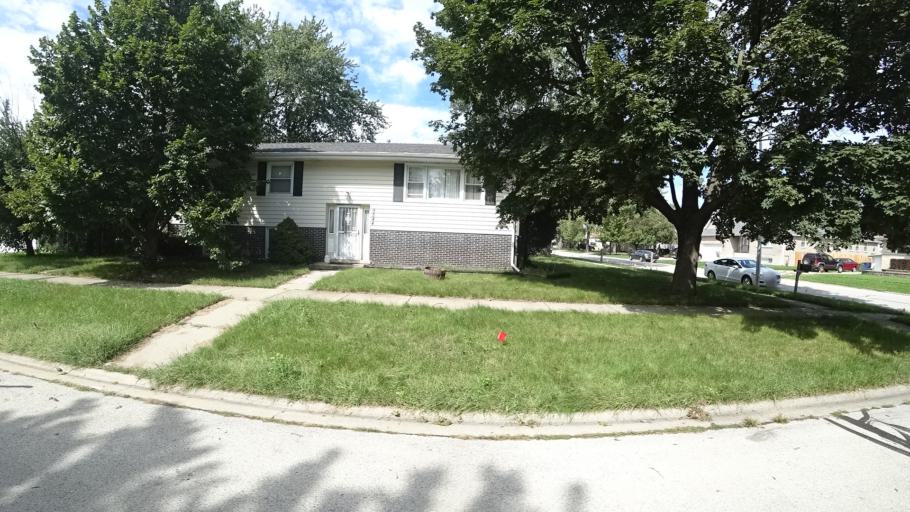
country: US
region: Illinois
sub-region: Cook County
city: Oak Lawn
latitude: 41.7178
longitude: -87.7727
